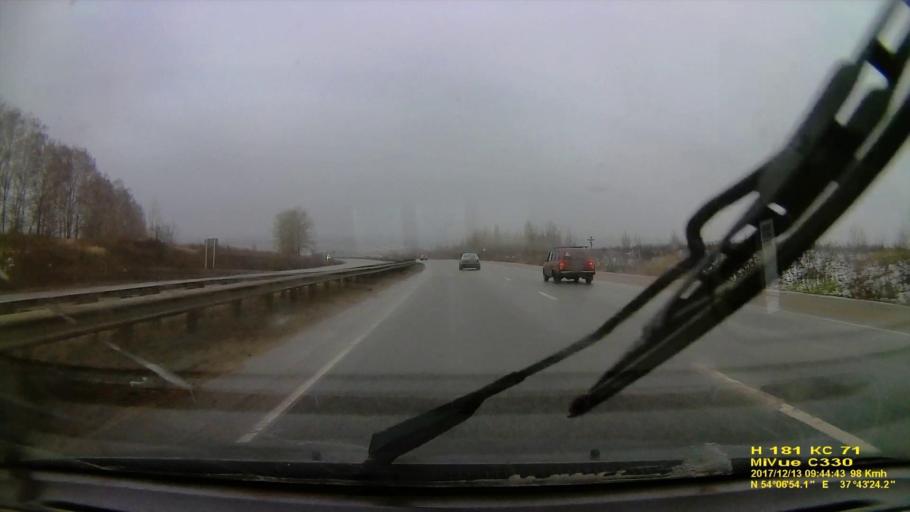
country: RU
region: Tula
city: Bolokhovo
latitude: 54.1152
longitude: 37.7242
